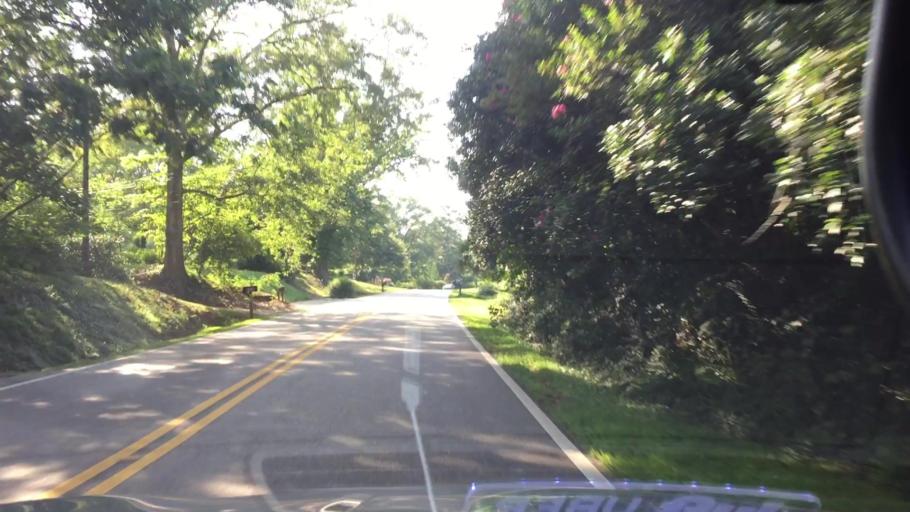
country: US
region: Alabama
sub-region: Lee County
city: Auburn
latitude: 32.5944
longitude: -85.4706
